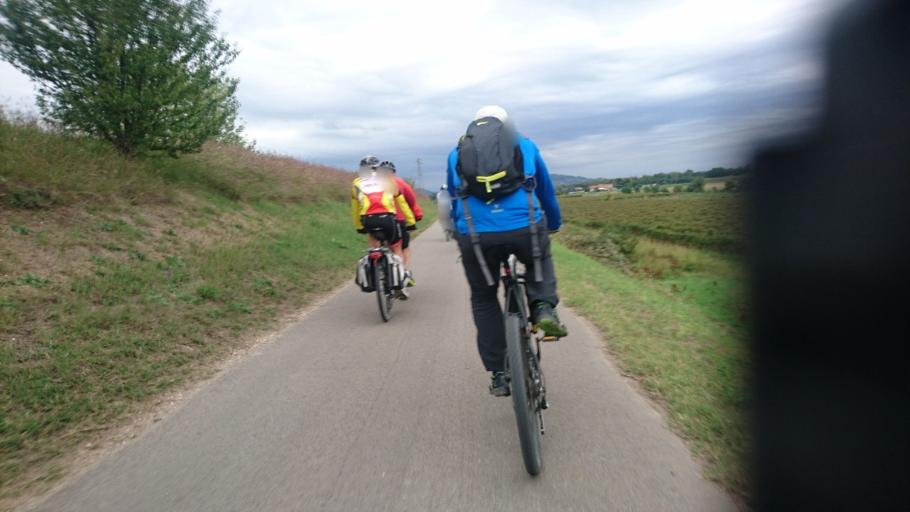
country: IT
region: Veneto
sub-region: Provincia di Vicenza
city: Montebello Vicentino
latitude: 45.4634
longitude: 11.3900
